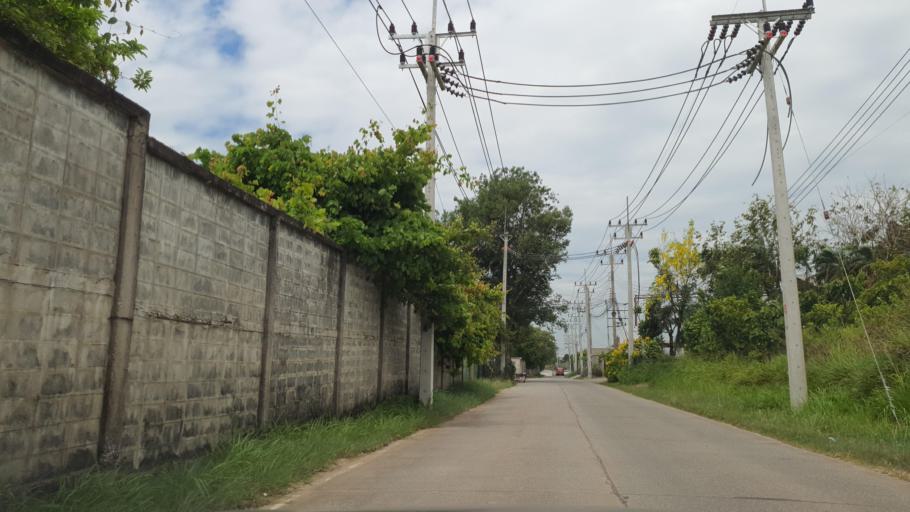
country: TH
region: Chon Buri
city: Bang Lamung
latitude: 12.9838
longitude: 100.9456
